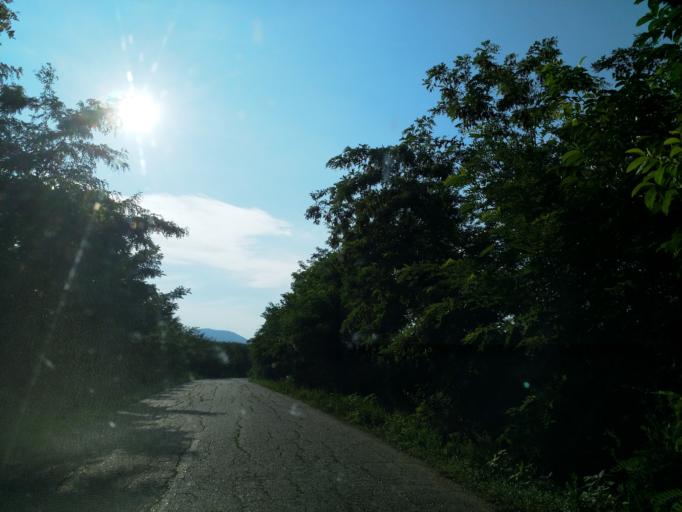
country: RS
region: Central Serbia
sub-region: Pomoravski Okrug
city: Jagodina
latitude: 43.9920
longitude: 21.2032
